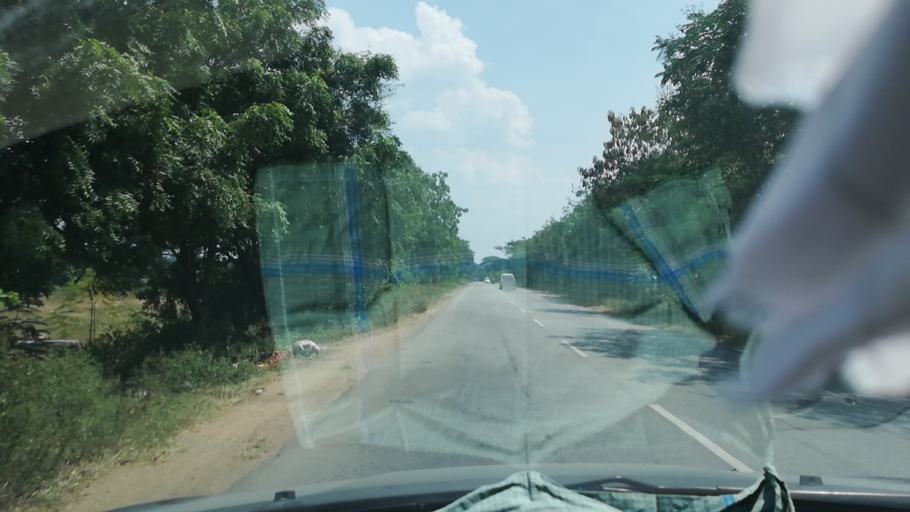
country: IN
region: Telangana
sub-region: Rangareddi
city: Secunderabad
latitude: 17.6357
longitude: 78.5590
